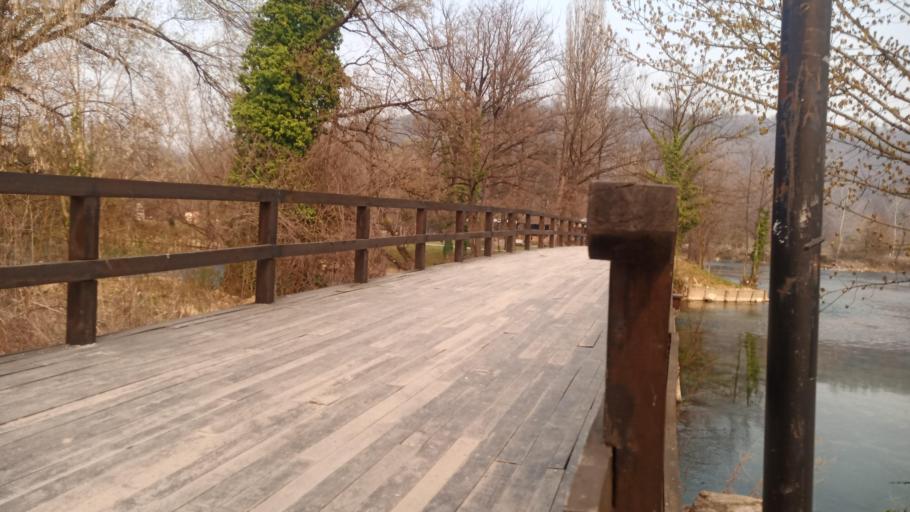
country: BA
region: Federation of Bosnia and Herzegovina
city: Bosanska Krupa
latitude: 44.8868
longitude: 16.1546
